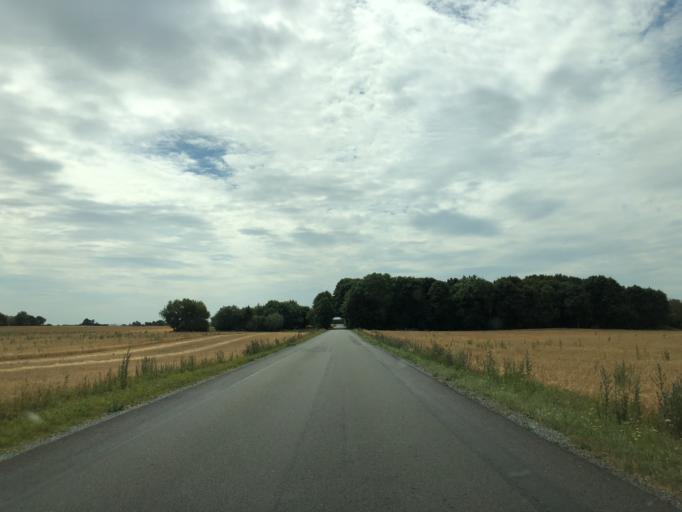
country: DK
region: South Denmark
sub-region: Vejle Kommune
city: Egtved
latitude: 55.6259
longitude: 9.1938
